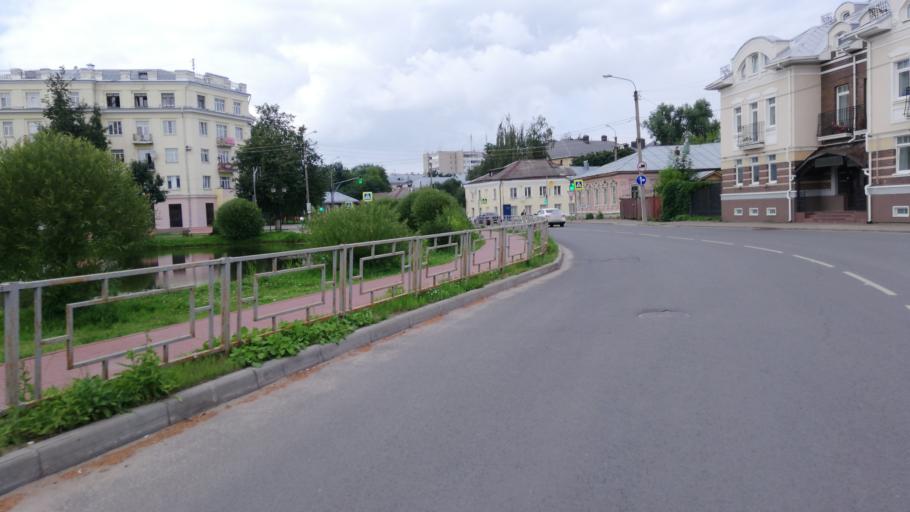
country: RU
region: Kostroma
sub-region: Kostromskoy Rayon
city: Kostroma
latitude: 57.7684
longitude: 40.9358
